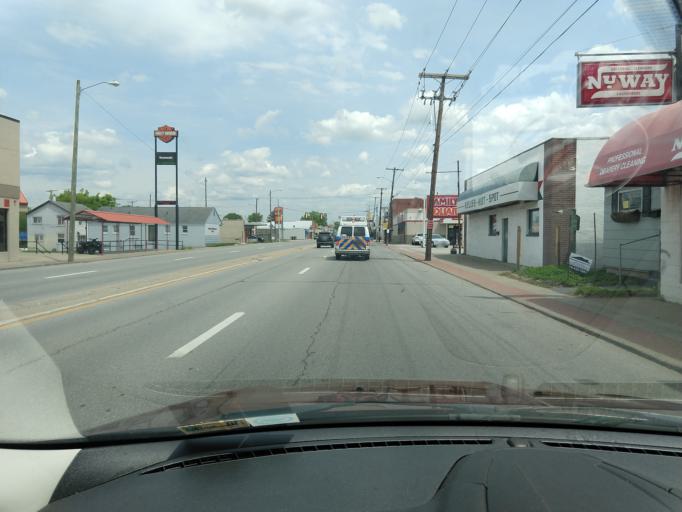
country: US
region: West Virginia
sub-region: Kanawha County
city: Dunbar
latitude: 38.3542
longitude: -81.7328
